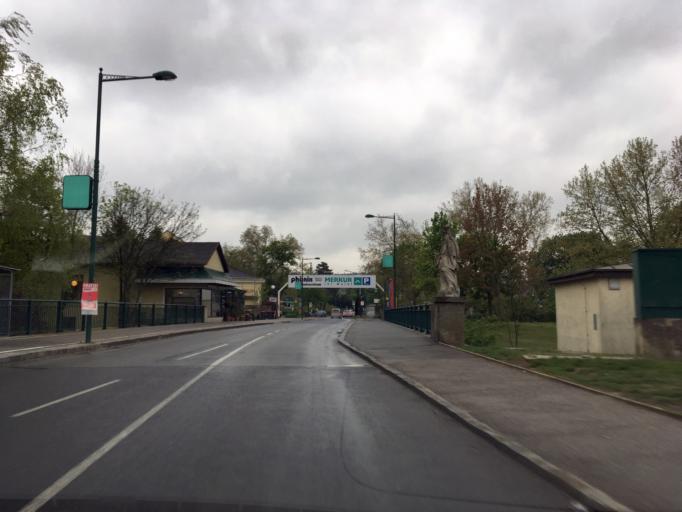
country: AT
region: Burgenland
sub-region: Politischer Bezirk Neusiedl am See
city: Bruckneudorf
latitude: 48.0210
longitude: 16.7775
